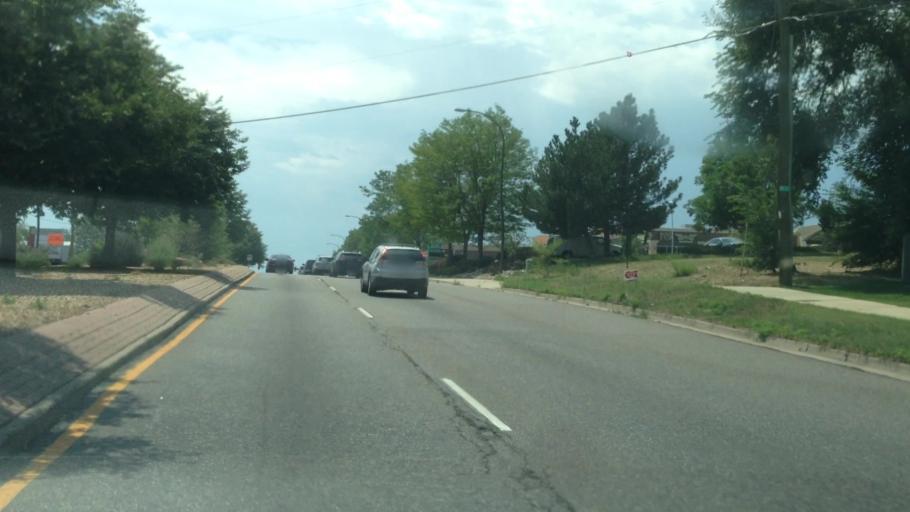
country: US
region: Colorado
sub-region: Jefferson County
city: Lakewood
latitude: 39.6989
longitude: -105.0816
